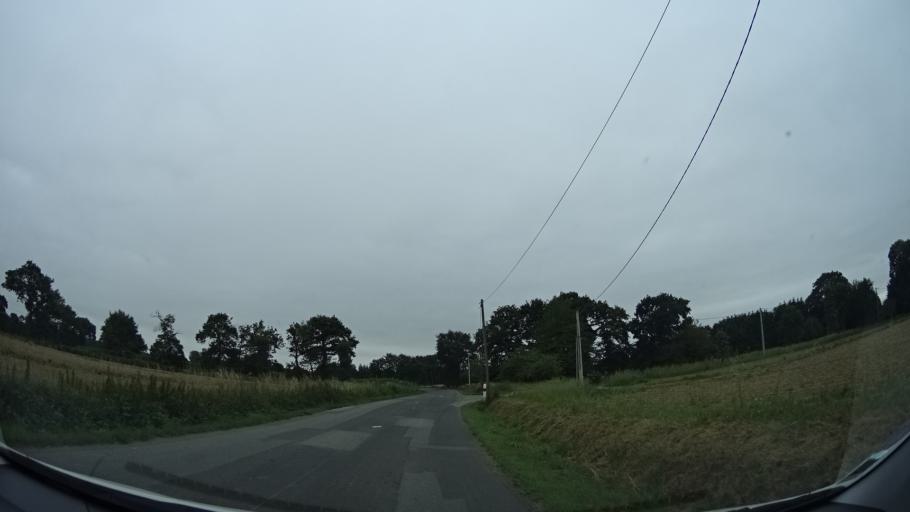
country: FR
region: Brittany
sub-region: Departement d'Ille-et-Vilaine
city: Hede-Bazouges
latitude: 48.2889
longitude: -1.7711
